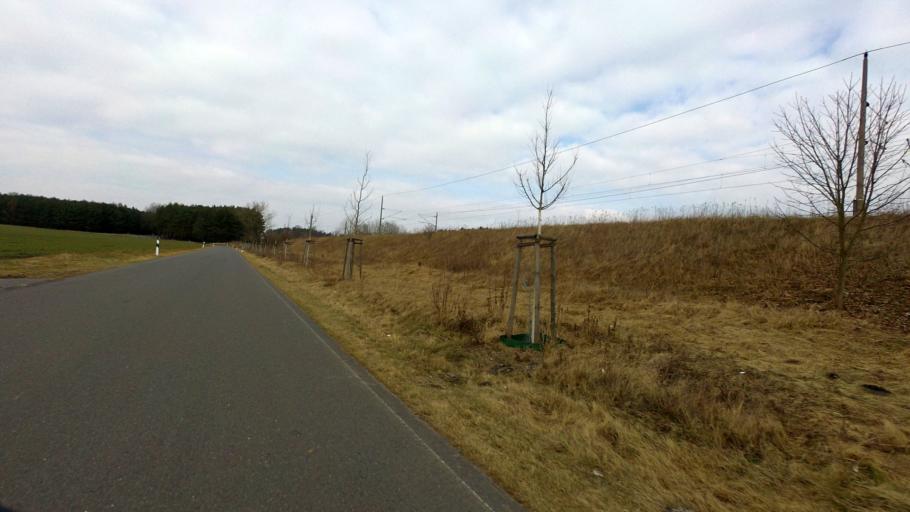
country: DE
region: Brandenburg
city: Ludwigsfelde
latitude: 52.2688
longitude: 13.2660
